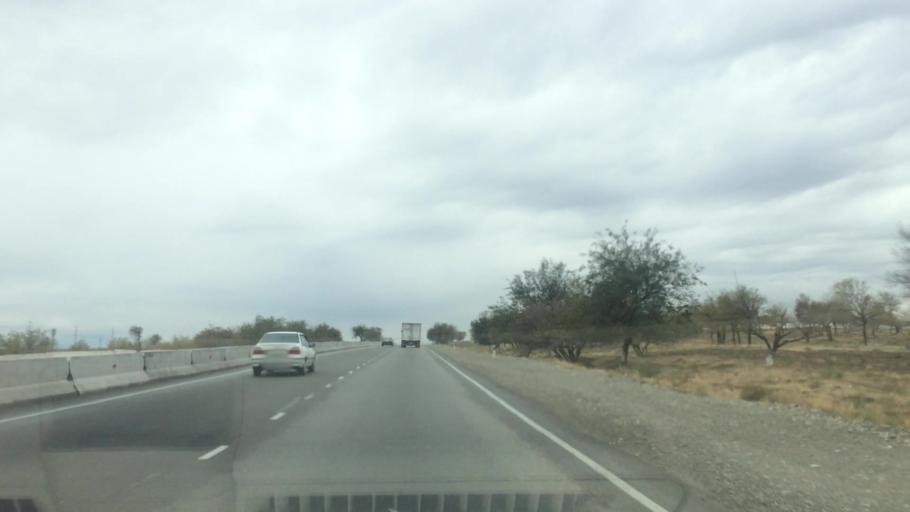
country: UZ
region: Samarqand
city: Bulung'ur
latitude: 39.9297
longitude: 67.5213
